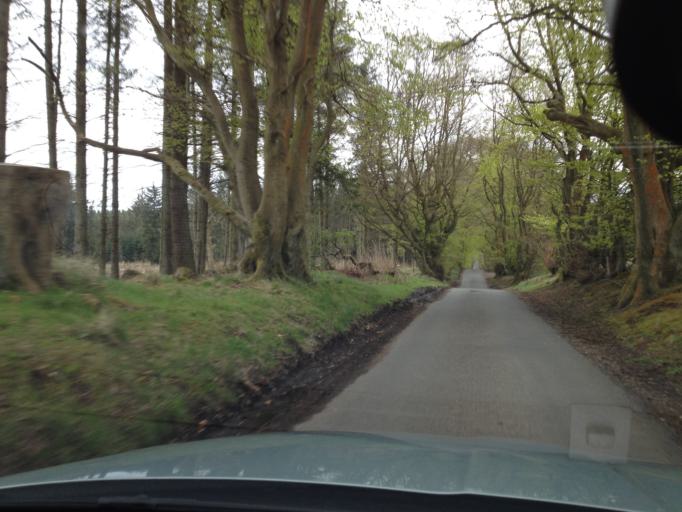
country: GB
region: Scotland
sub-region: West Lothian
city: Linlithgow
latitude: 55.9475
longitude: -3.6046
